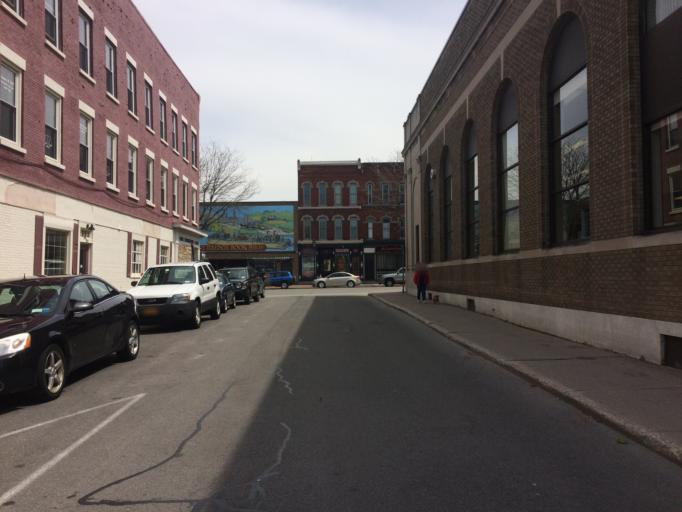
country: US
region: New York
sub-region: Monroe County
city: Brockport
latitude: 43.2154
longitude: -77.9392
